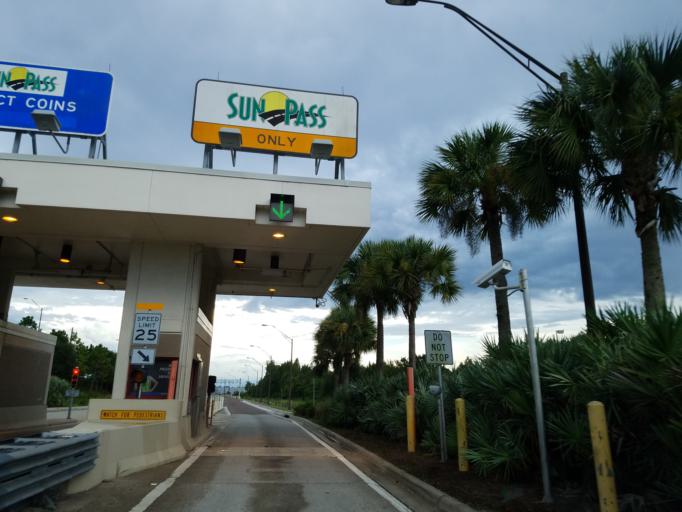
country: US
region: Florida
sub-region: Pasco County
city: Odessa
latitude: 28.1878
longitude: -82.5438
